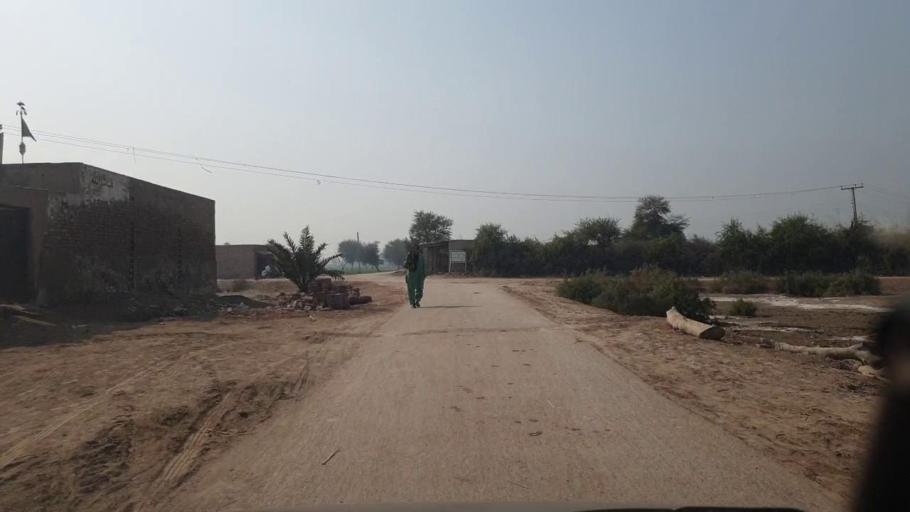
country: PK
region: Sindh
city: Shahdadpur
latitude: 26.0245
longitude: 68.5420
